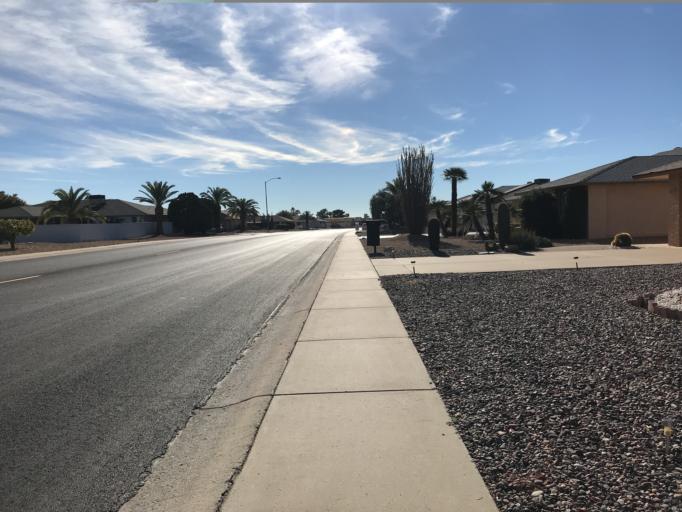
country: US
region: Arizona
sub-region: Maricopa County
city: Sun City West
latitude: 33.6667
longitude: -112.3274
